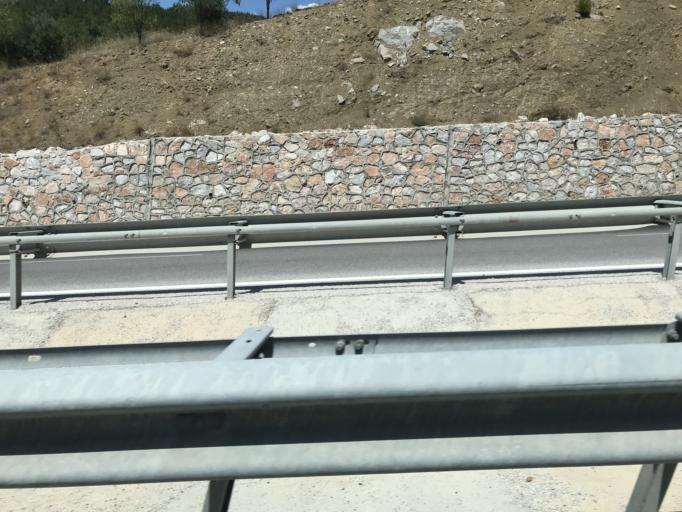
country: TR
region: Balikesir
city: Golcuk
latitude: 39.3567
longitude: 27.9546
